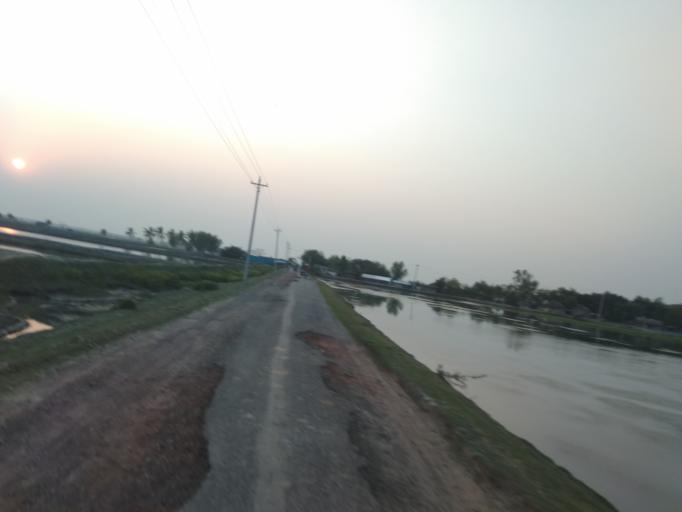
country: IN
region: West Bengal
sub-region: North 24 Parganas
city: Taki
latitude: 22.4560
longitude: 89.0752
